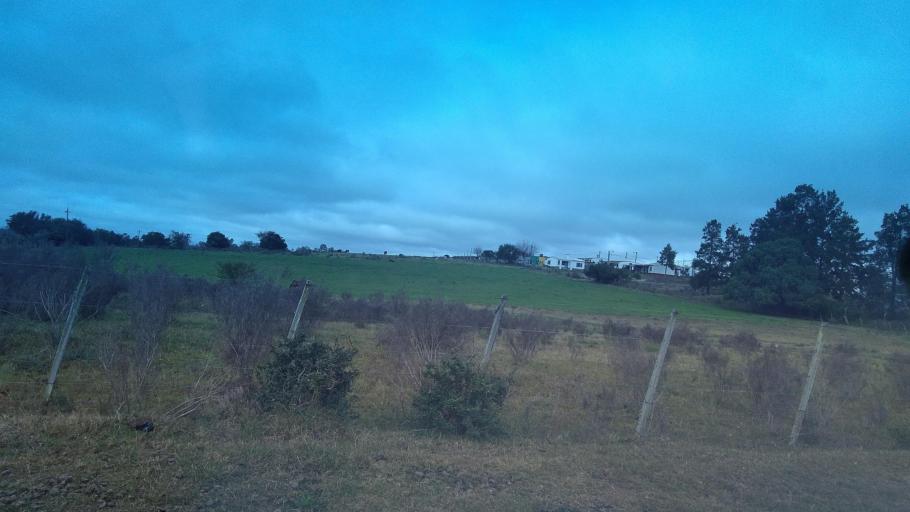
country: UY
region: Canelones
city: Tala
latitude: -34.2051
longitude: -55.7404
